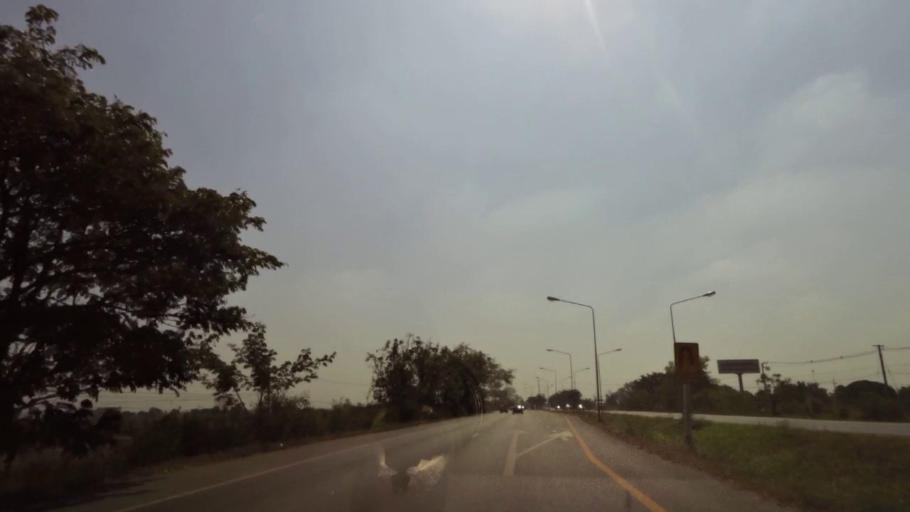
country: TH
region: Phichit
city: Wachira Barami
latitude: 16.4722
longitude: 100.1473
